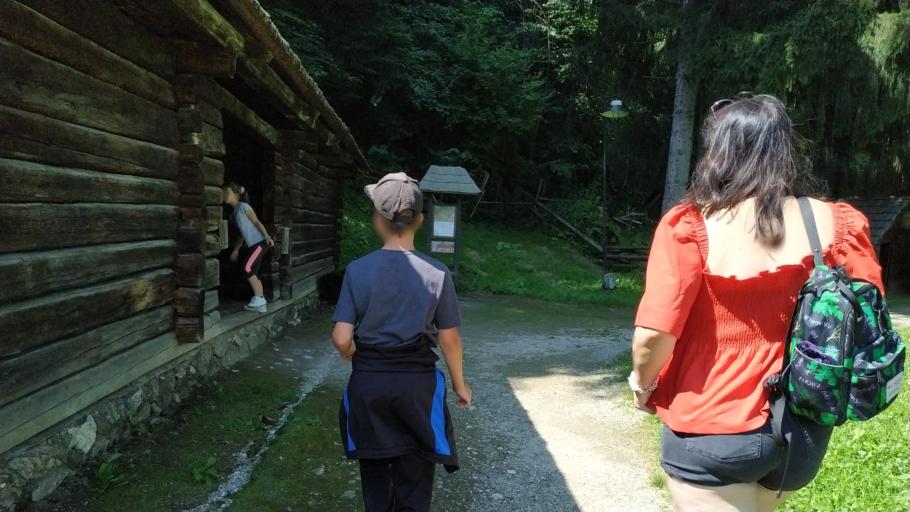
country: RO
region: Brasov
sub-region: Comuna Bran
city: Bran
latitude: 45.5147
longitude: 25.3702
